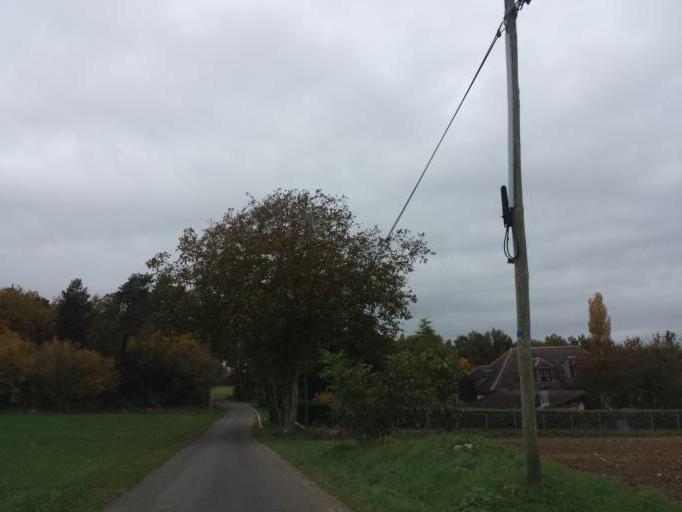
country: FR
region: Poitou-Charentes
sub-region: Departement de la Charente
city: Puymoyen
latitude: 45.5997
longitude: 0.1780
